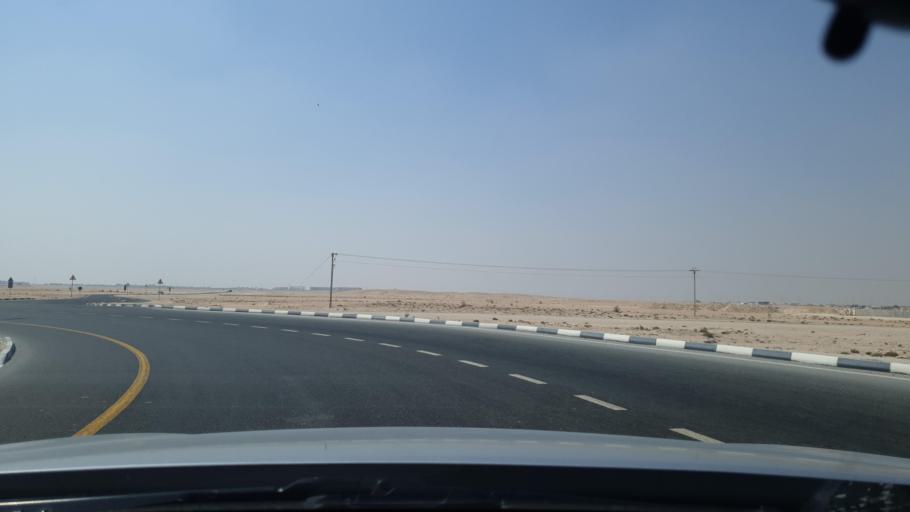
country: QA
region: Al Khawr
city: Al Khawr
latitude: 25.6730
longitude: 51.4700
